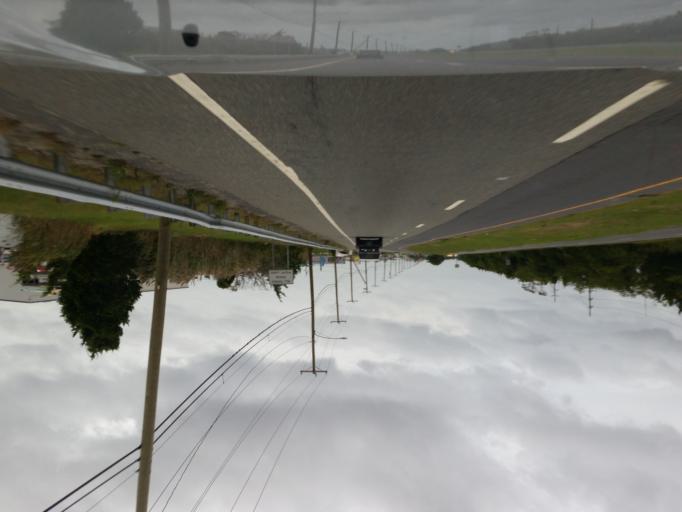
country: US
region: New Jersey
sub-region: Cape May County
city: Wildwood Crest
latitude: 38.9995
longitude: -74.8524
